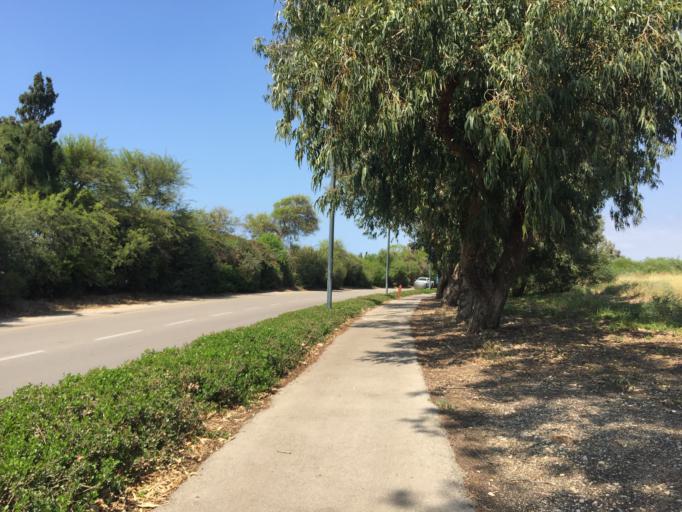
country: IL
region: Haifa
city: Qesarya
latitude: 32.4999
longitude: 34.9040
